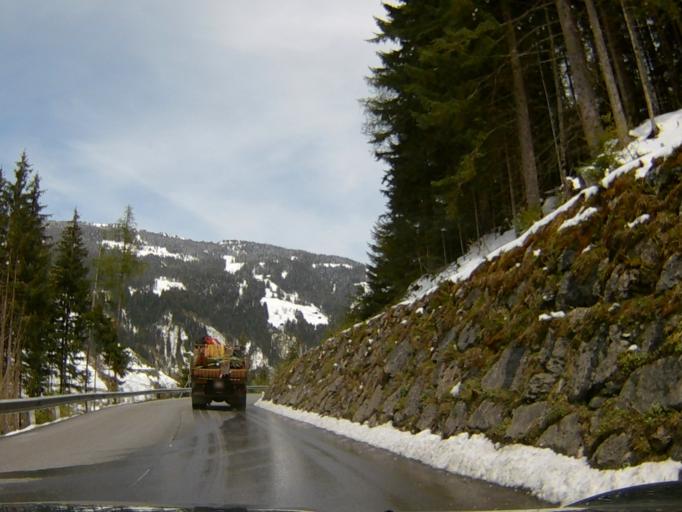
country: AT
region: Tyrol
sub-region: Politischer Bezirk Schwaz
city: Gerlosberg
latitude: 47.2134
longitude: 11.9314
